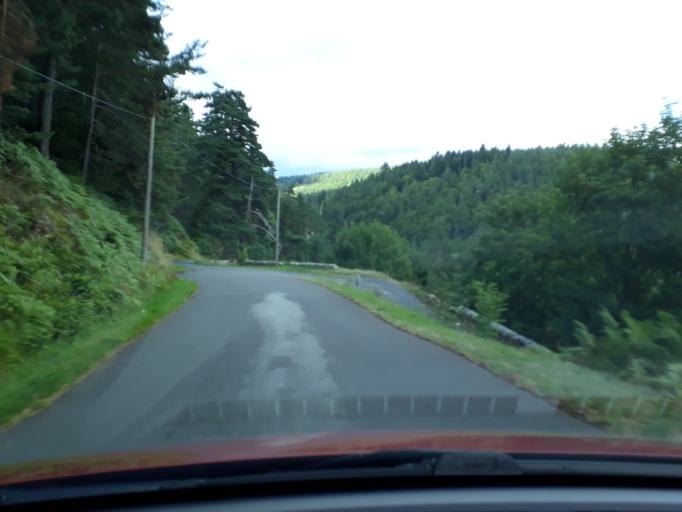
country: FR
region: Auvergne
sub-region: Departement de la Haute-Loire
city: Le Monastier-sur-Gazeille
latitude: 44.8217
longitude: 3.9431
